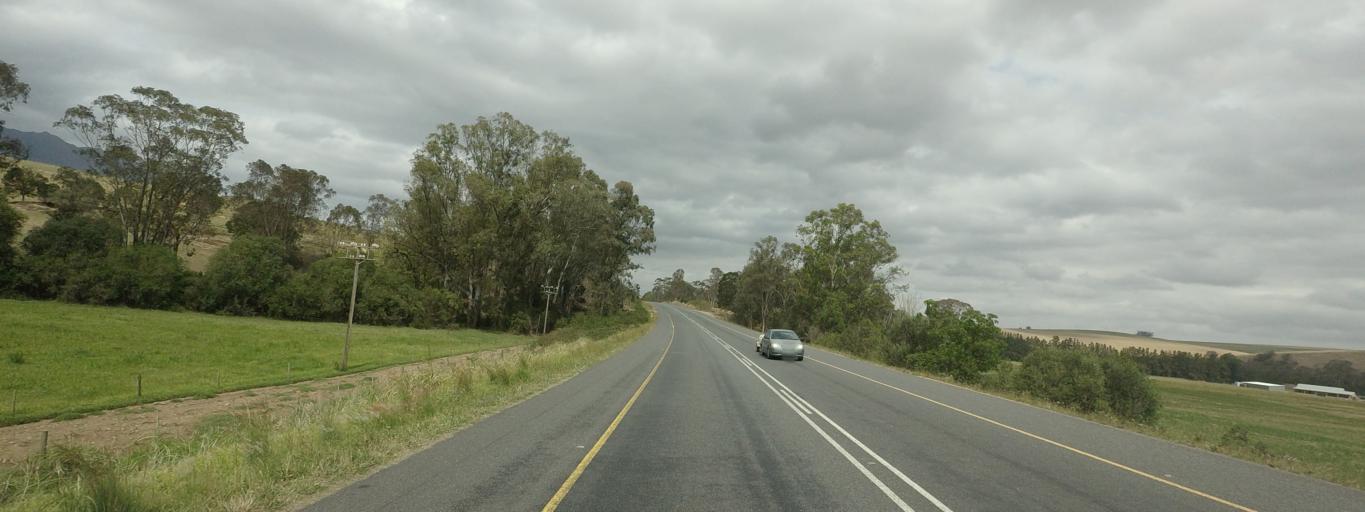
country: ZA
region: Western Cape
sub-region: Overberg District Municipality
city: Swellendam
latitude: -34.0144
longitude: 20.3962
